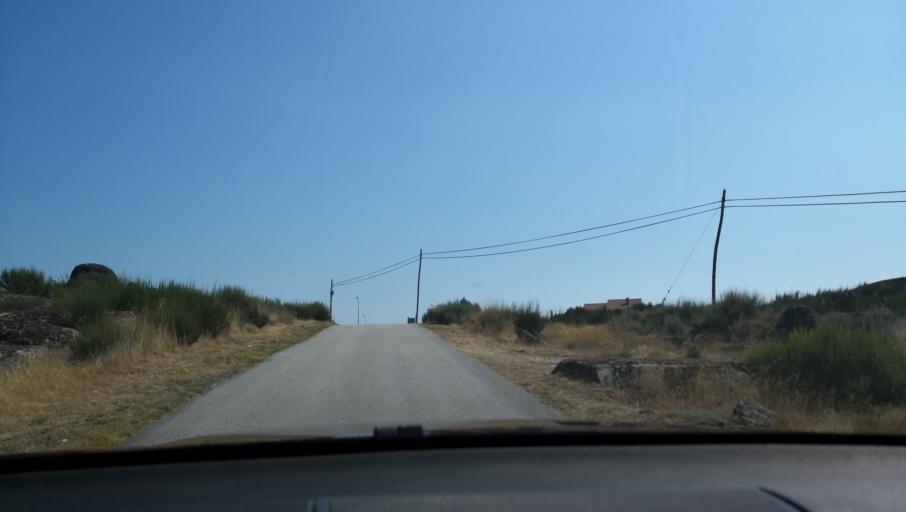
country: PT
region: Vila Real
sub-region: Sabrosa
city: Sabrosa
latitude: 41.2952
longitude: -7.6128
